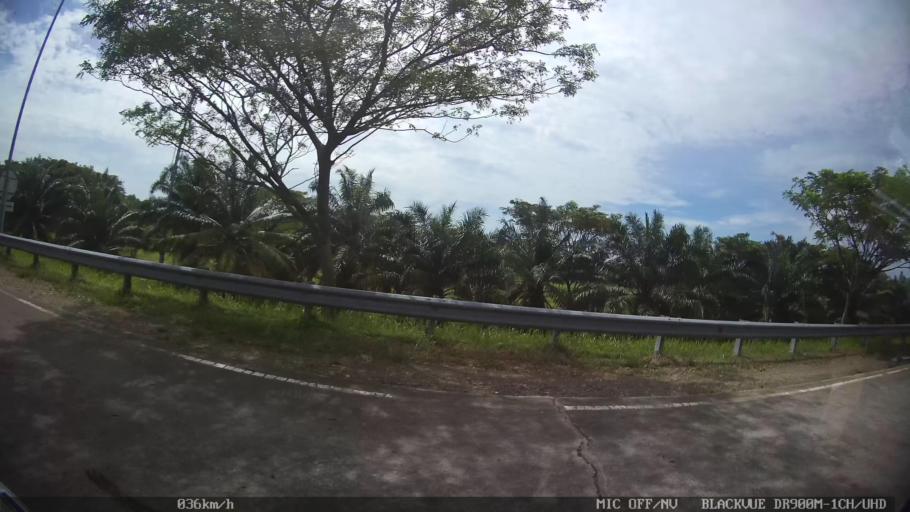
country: ID
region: North Sumatra
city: Percut
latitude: 3.6314
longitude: 98.8777
